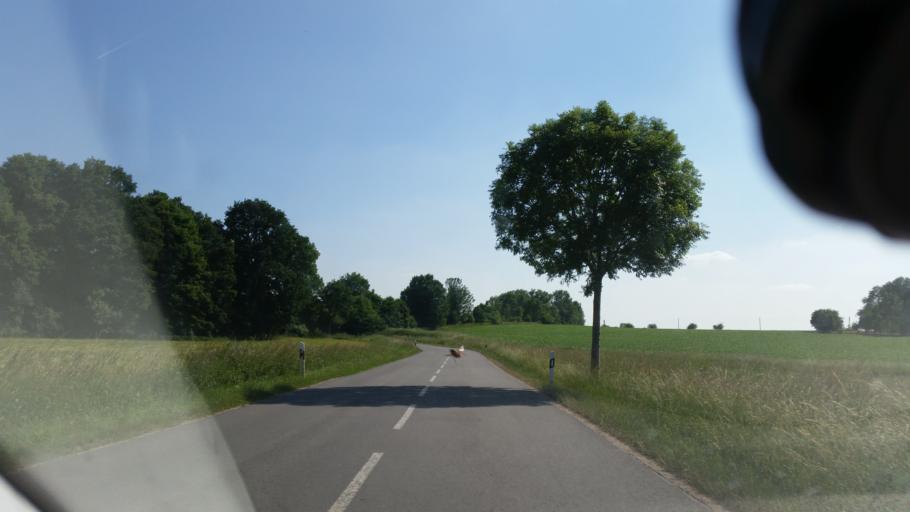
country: DE
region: Lower Saxony
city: Konigslutter am Elm
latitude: 52.3328
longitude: 10.8017
